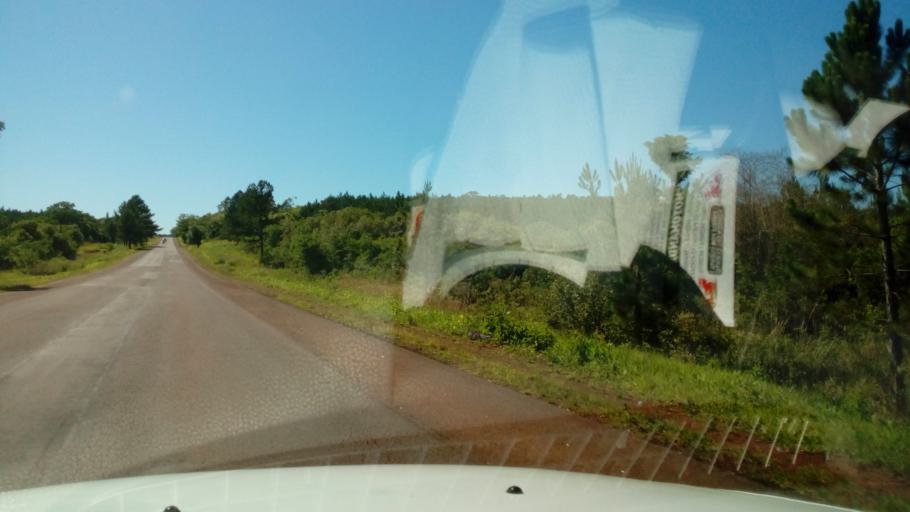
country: AR
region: Misiones
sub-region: Departamento de Leandro N. Alem
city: Leandro N. Alem
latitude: -27.5763
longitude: -55.3817
